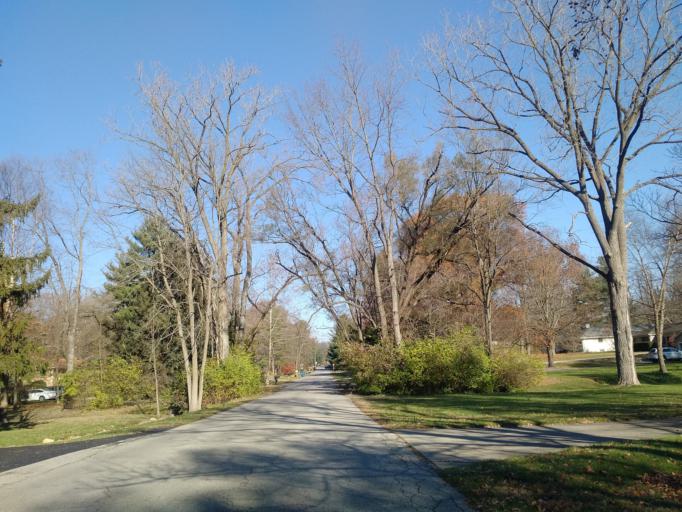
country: US
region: Indiana
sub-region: Marion County
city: Meridian Hills
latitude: 39.9147
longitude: -86.1233
